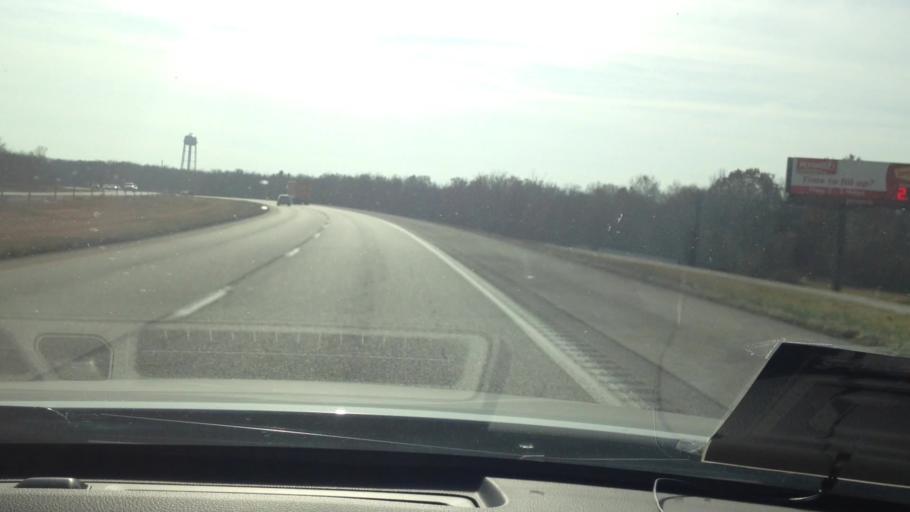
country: US
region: Missouri
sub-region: Cass County
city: Raymore
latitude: 38.7656
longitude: -94.4907
